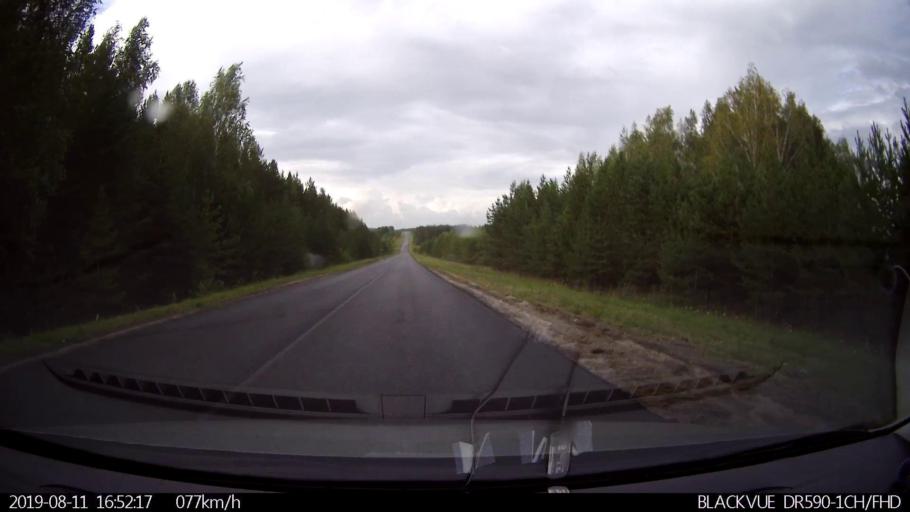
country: RU
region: Ulyanovsk
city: Mayna
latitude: 54.2461
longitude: 47.6747
